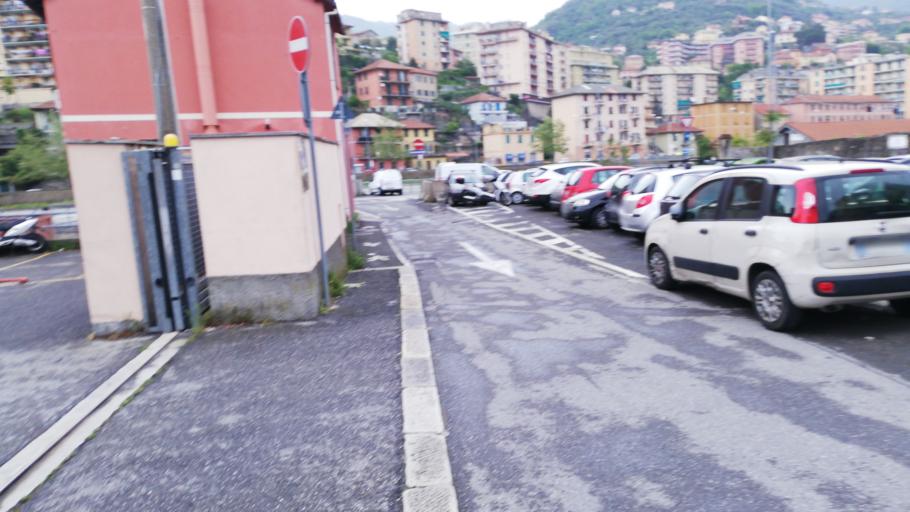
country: IT
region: Liguria
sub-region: Provincia di Genova
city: Piccarello
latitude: 44.4475
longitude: 9.0093
